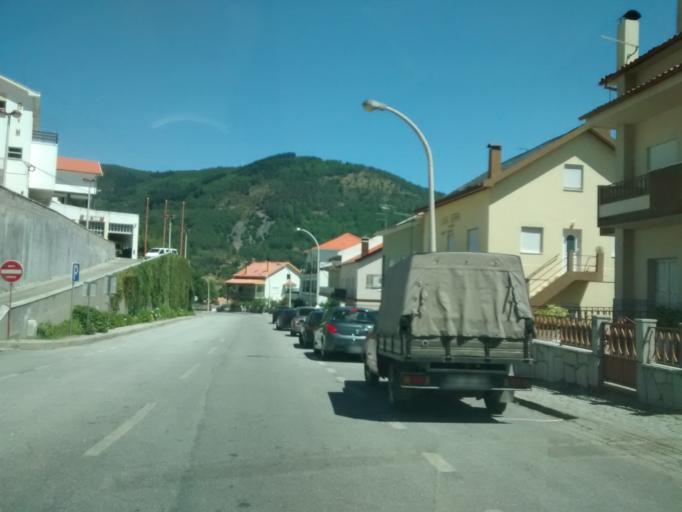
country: PT
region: Guarda
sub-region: Manteigas
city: Manteigas
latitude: 40.4032
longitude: -7.5354
